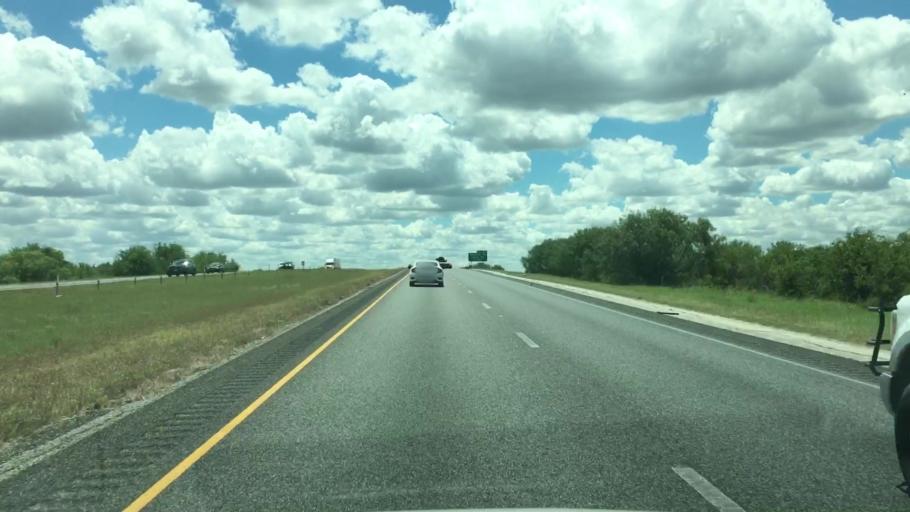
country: US
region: Texas
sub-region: Bexar County
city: Elmendorf
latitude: 29.2927
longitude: -98.3953
